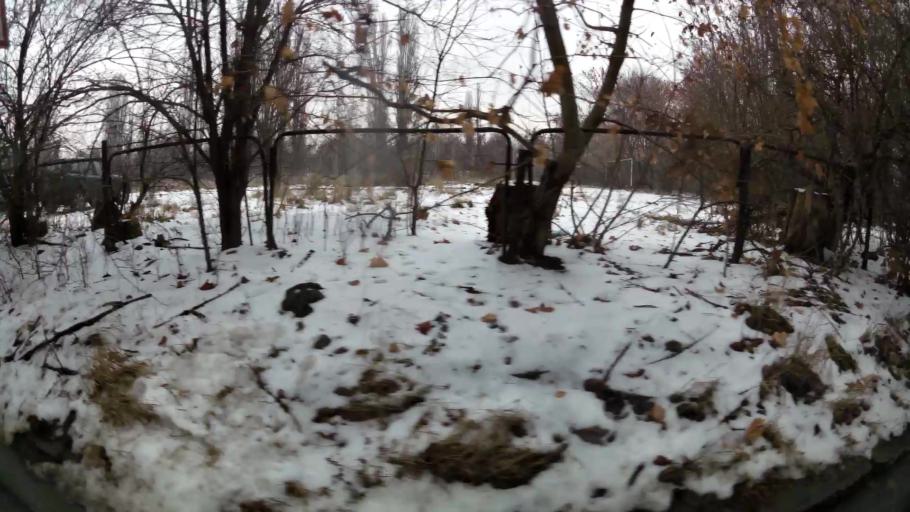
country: BG
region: Sofia-Capital
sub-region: Stolichna Obshtina
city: Sofia
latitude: 42.6883
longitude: 23.2948
